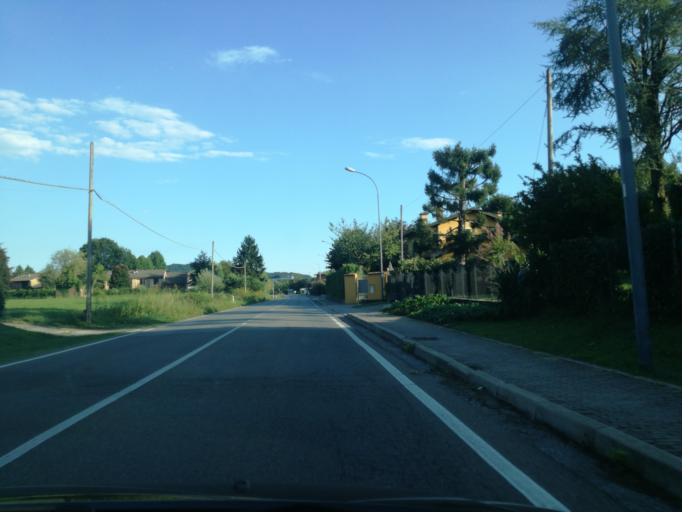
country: IT
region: Lombardy
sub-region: Provincia di Lecco
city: Arlate
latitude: 45.7255
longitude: 9.4428
